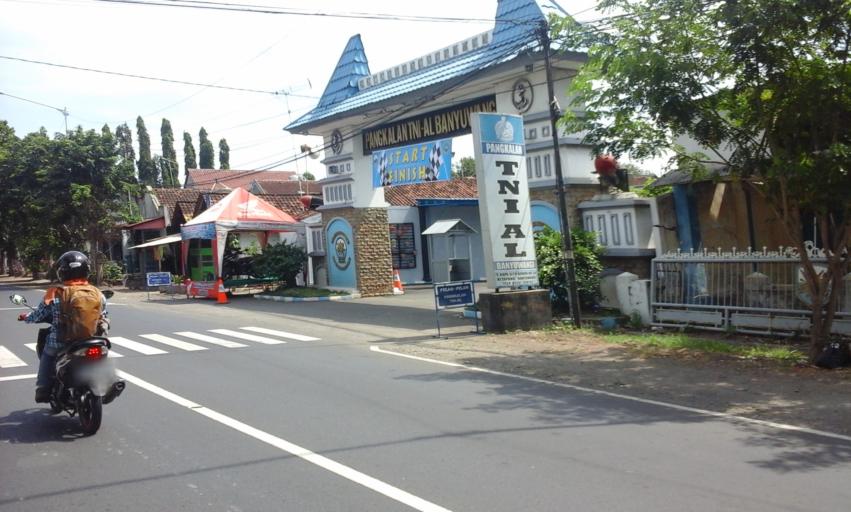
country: ID
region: East Java
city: Klatakan
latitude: -8.1387
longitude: 114.3987
